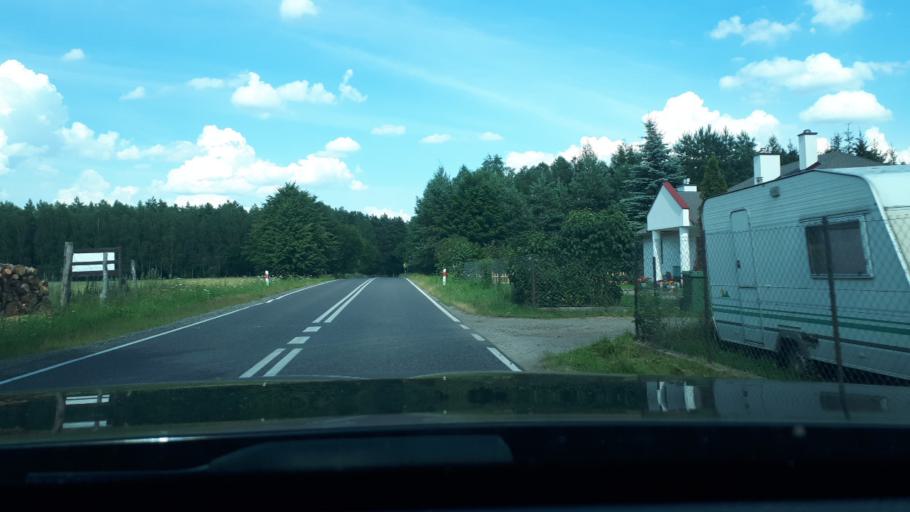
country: PL
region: Warmian-Masurian Voivodeship
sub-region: Powiat olsztynski
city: Stawiguda
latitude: 53.5284
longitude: 20.4500
